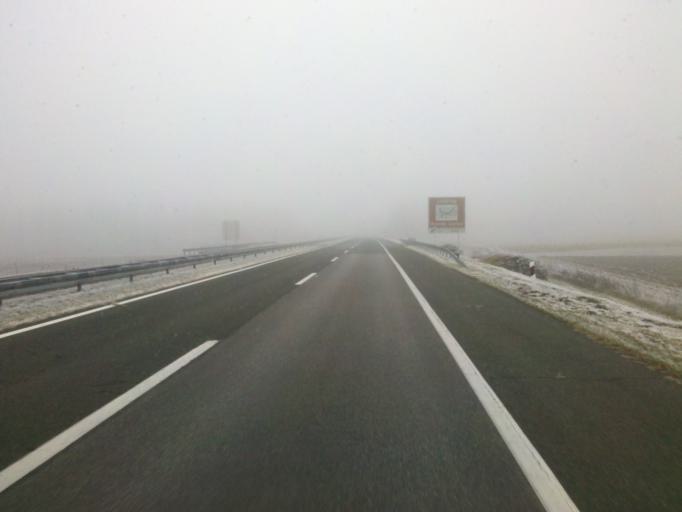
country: HR
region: Medimurska
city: Orehovica
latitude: 46.3217
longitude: 16.5148
